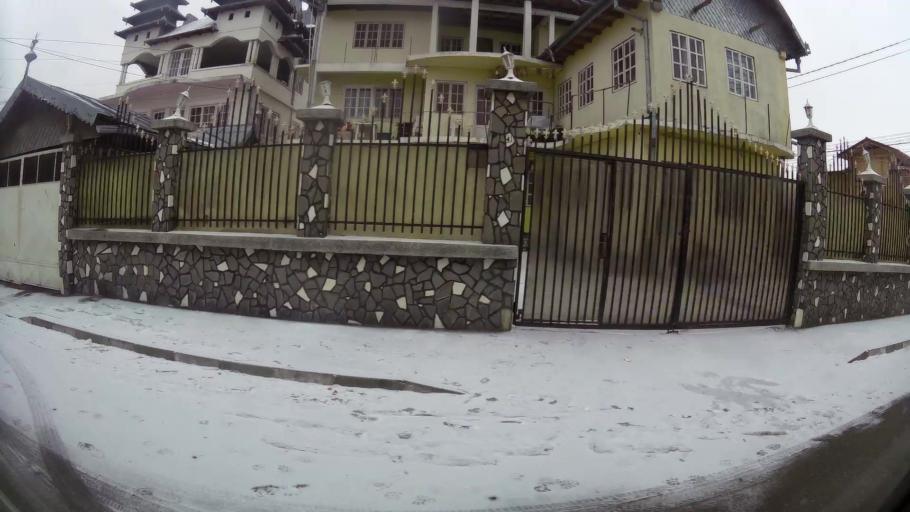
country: RO
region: Prahova
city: Ploiesti
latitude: 44.9541
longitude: 26.0147
